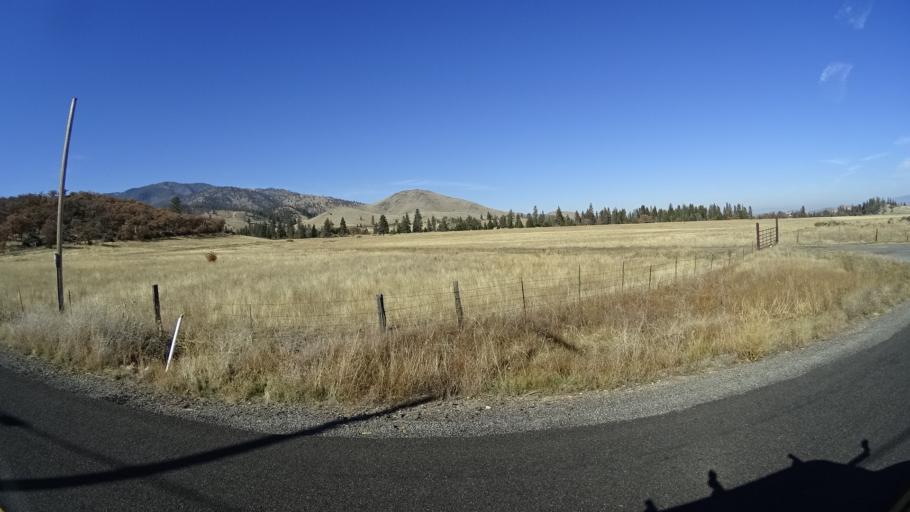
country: US
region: California
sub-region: Siskiyou County
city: Weed
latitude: 41.4377
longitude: -122.4514
